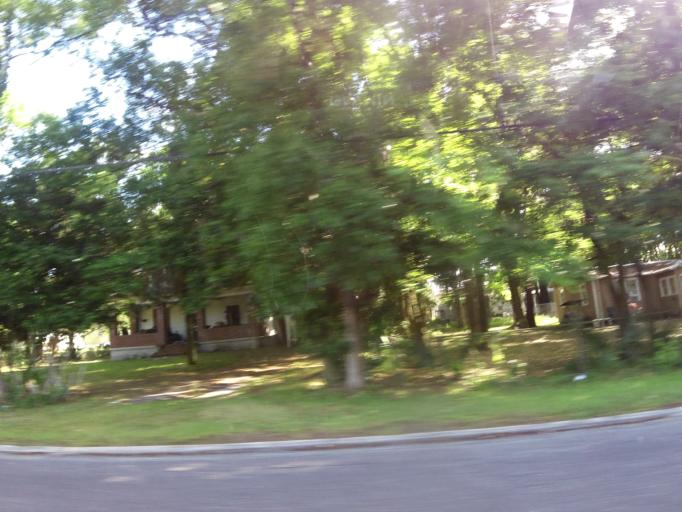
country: US
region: Florida
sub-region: Nassau County
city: Callahan
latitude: 30.5585
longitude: -81.8292
